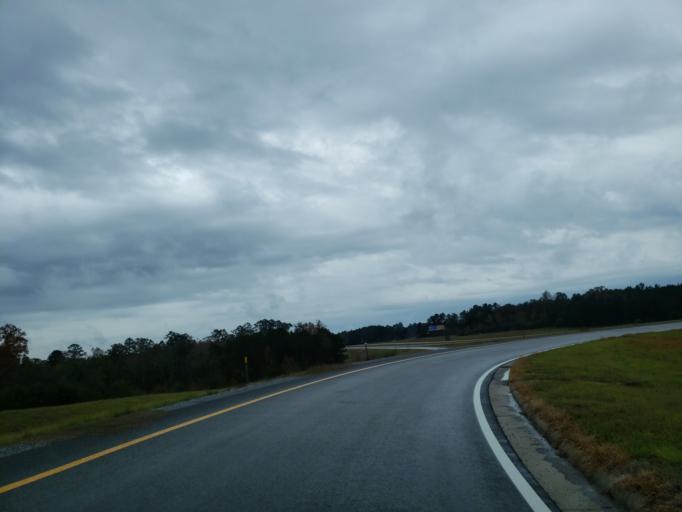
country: US
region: Mississippi
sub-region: Wayne County
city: Waynesboro
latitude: 31.7075
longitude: -88.6241
